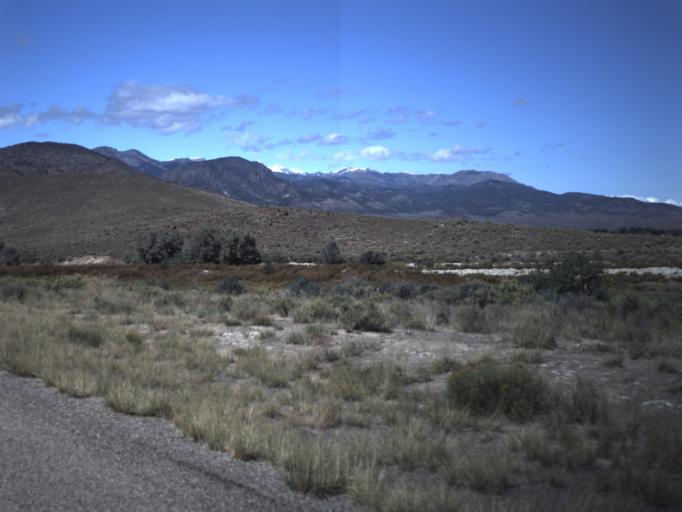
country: US
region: Utah
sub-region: Piute County
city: Junction
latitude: 38.2095
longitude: -112.2162
